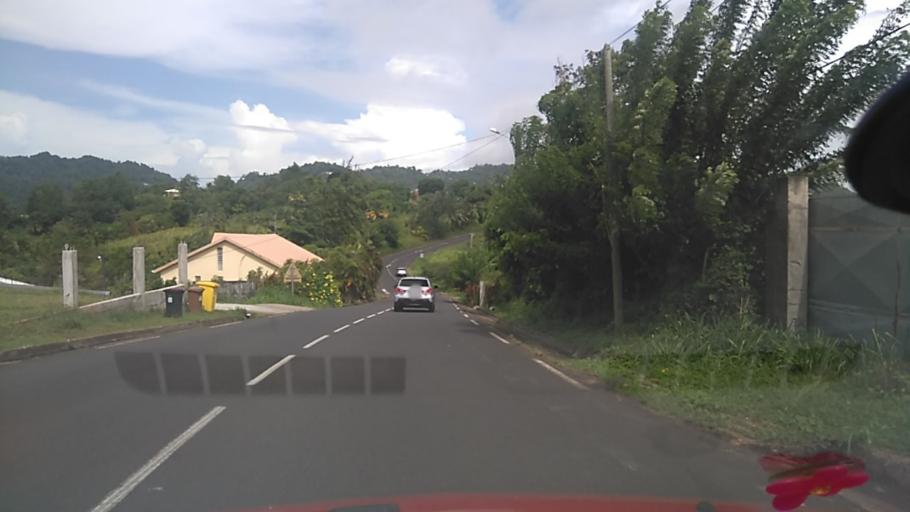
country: MQ
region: Martinique
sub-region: Martinique
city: Le Francois
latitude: 14.5938
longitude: -60.9217
